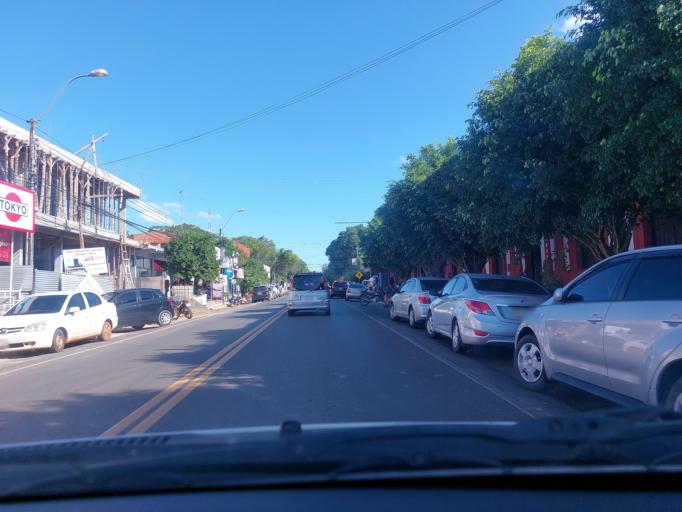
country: PY
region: San Pedro
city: Guayaybi
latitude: -24.6648
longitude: -56.4441
